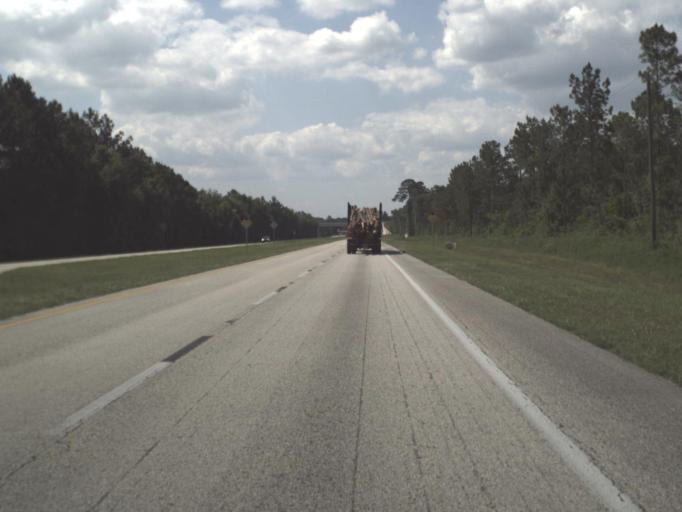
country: US
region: Florida
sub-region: Alachua County
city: Waldo
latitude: 29.7080
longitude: -82.1360
